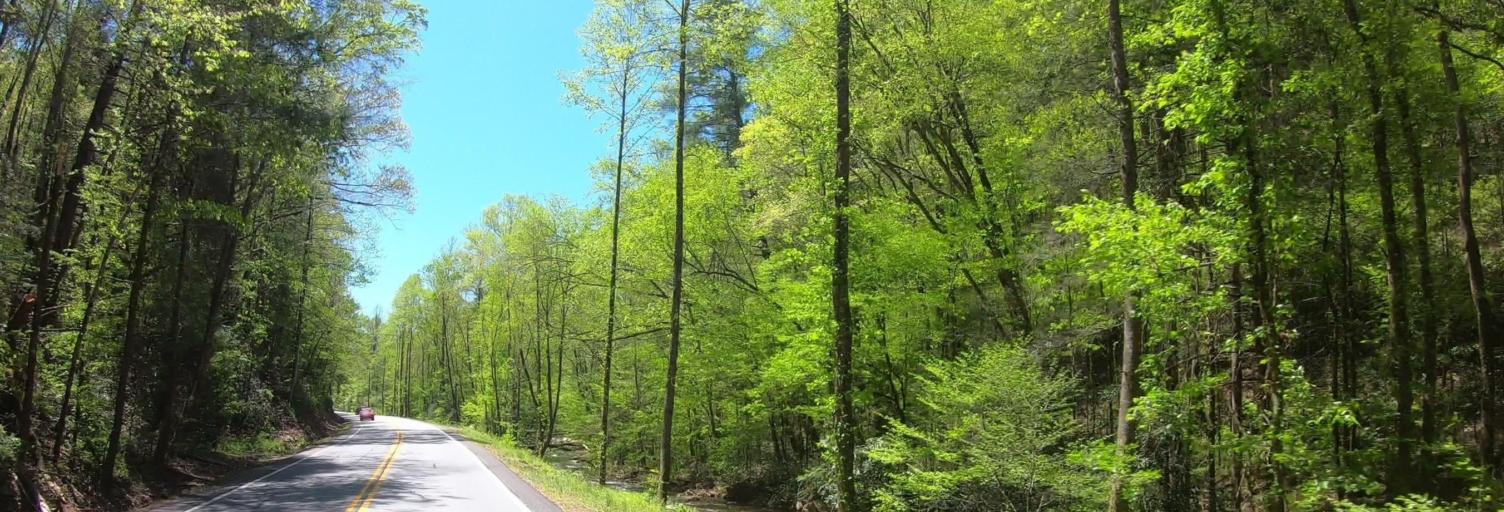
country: US
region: Georgia
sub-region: White County
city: Cleveland
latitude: 34.7428
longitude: -83.7502
